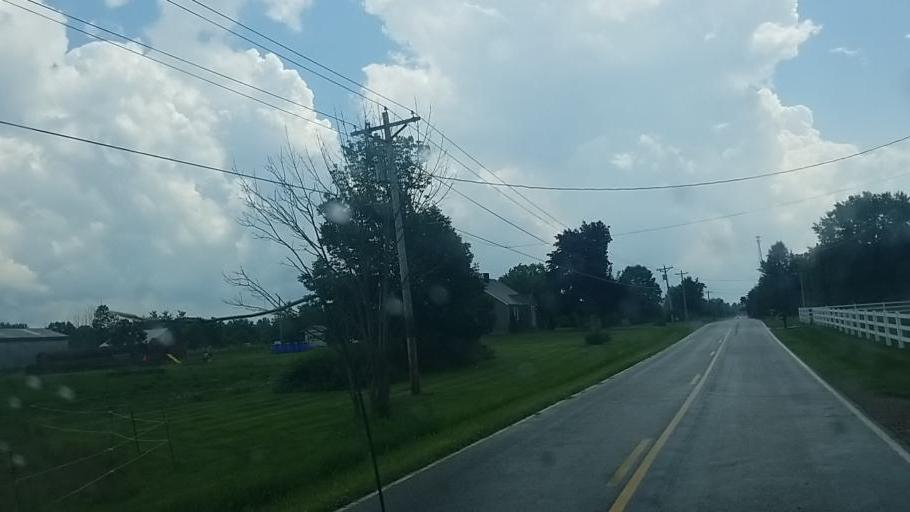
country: US
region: Ohio
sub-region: Lorain County
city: Grafton
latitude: 41.1760
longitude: -82.0036
